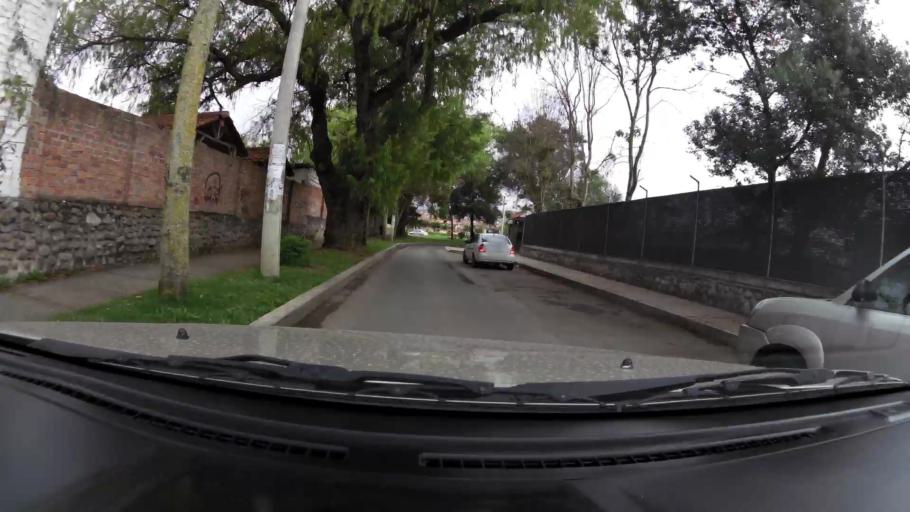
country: EC
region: Azuay
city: Cuenca
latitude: -2.9097
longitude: -78.9898
